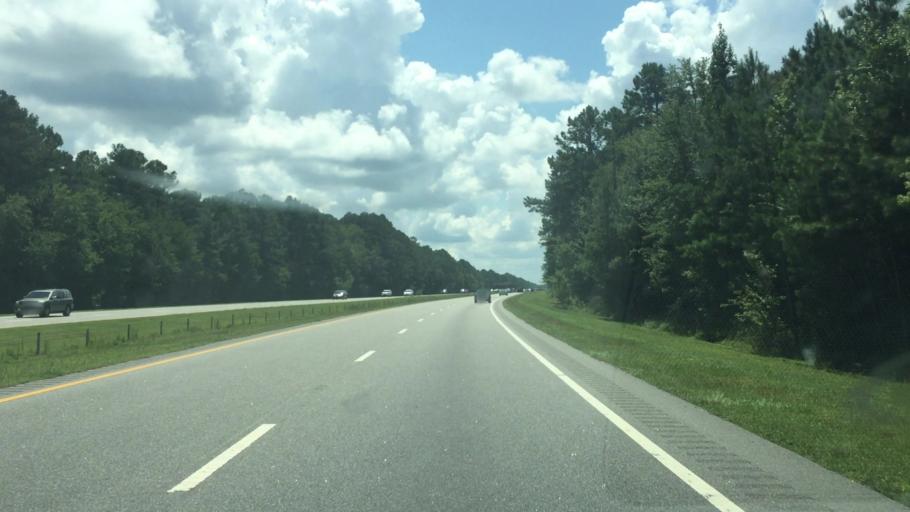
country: US
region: North Carolina
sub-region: Robeson County
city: Lumberton
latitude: 34.5654
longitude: -79.0287
